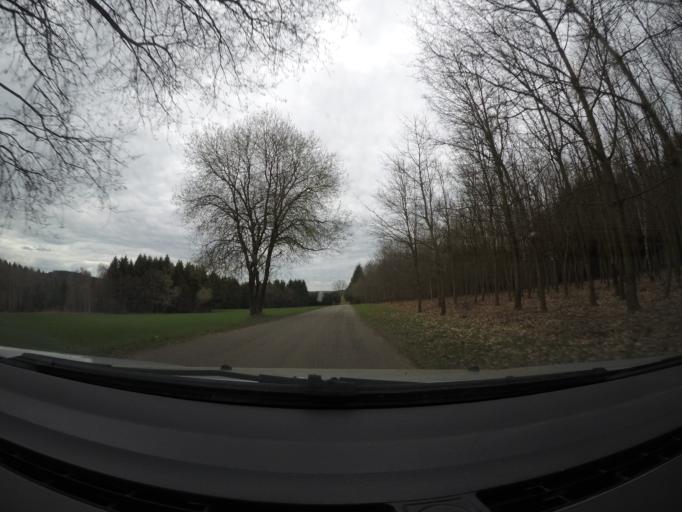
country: BE
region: Wallonia
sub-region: Province du Luxembourg
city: Leglise
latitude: 49.7784
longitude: 5.5833
